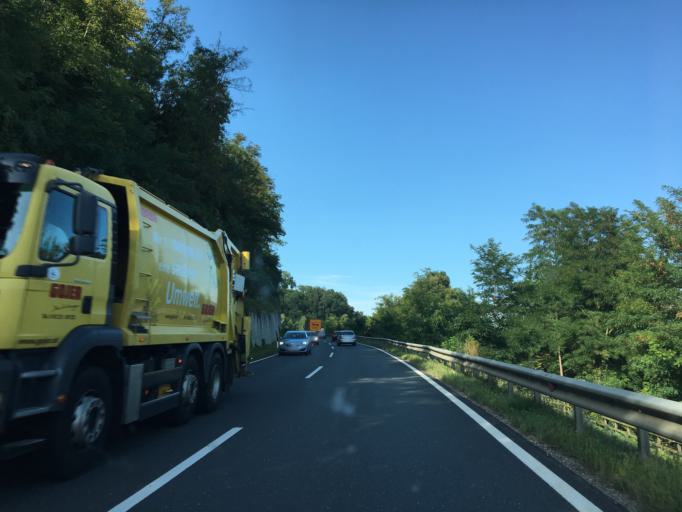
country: AT
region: Carinthia
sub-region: Politischer Bezirk Volkermarkt
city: Voelkermarkt
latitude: 46.6527
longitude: 14.6309
